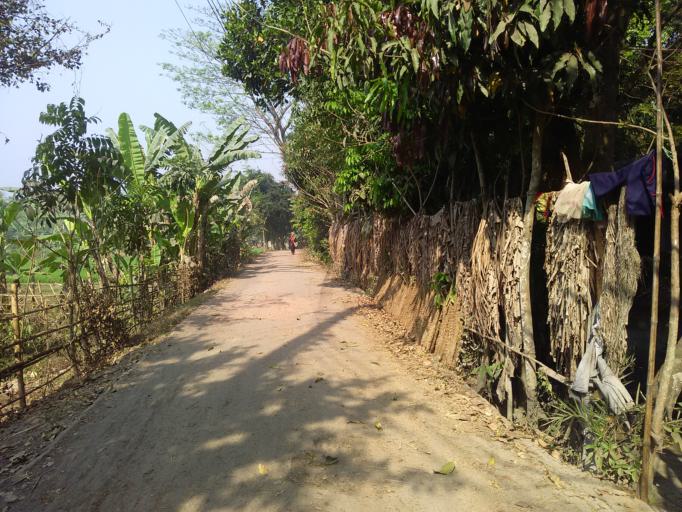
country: BD
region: Khulna
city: Khulna
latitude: 22.8964
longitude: 89.5317
